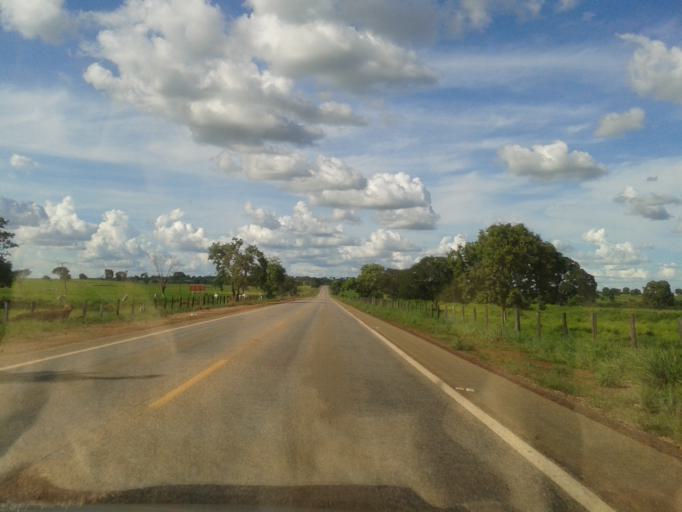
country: BR
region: Goias
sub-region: Mozarlandia
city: Mozarlandia
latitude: -14.7104
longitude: -50.5460
